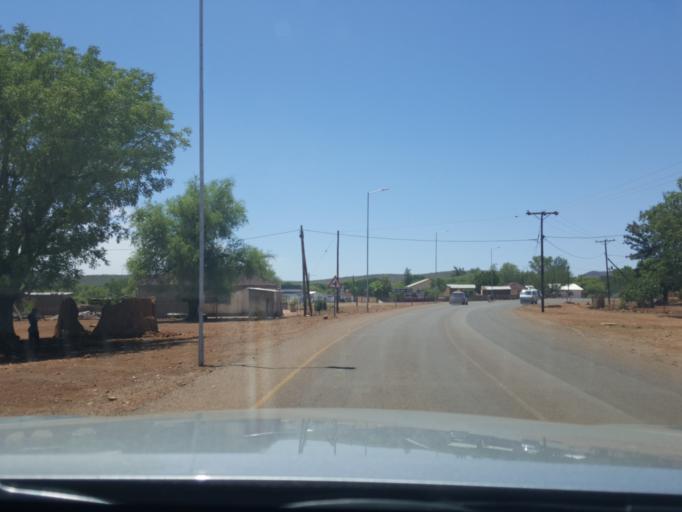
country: BW
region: South East
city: Ramotswa
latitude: -24.8700
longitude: 25.8788
